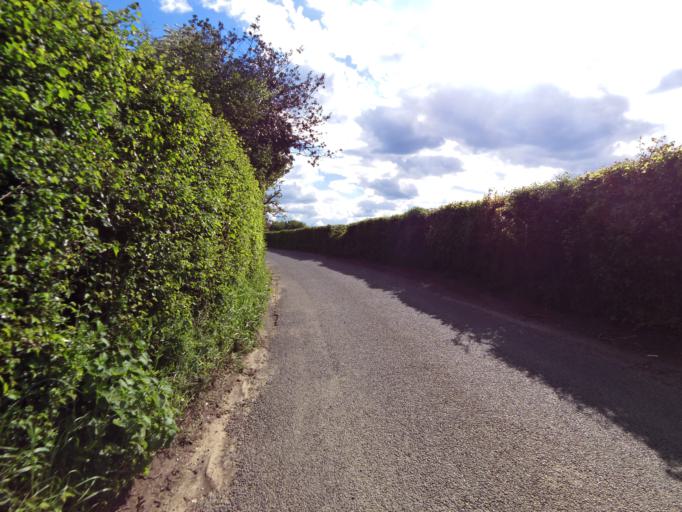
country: GB
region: England
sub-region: Suffolk
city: Woolpit
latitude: 52.2270
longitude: 0.8569
